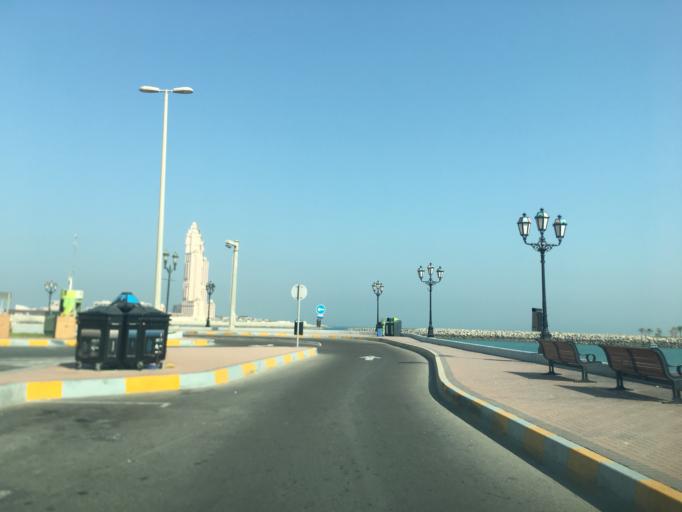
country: AE
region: Abu Dhabi
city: Abu Dhabi
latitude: 24.4785
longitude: 54.3328
